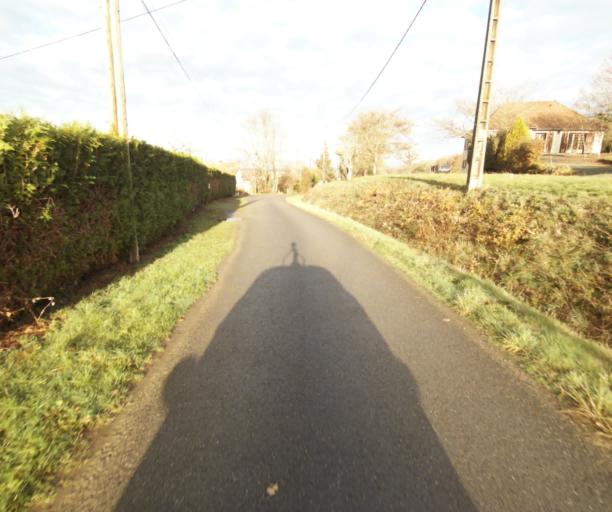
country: FR
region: Limousin
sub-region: Departement de la Correze
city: Saint-Mexant
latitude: 45.2583
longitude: 1.6293
